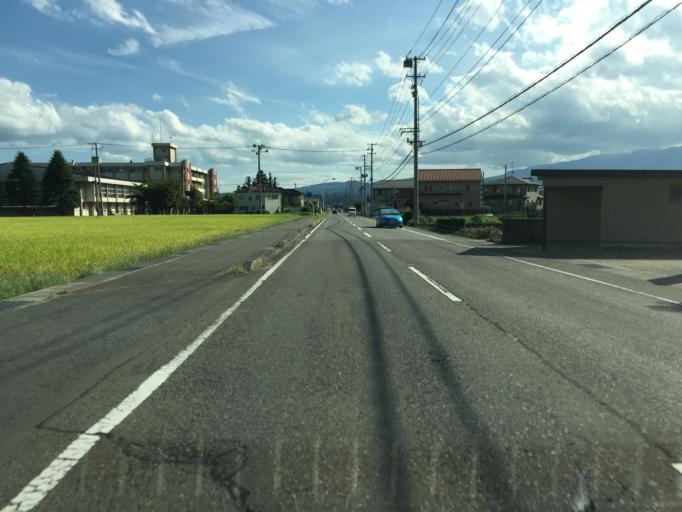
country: JP
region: Fukushima
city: Fukushima-shi
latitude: 37.7628
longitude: 140.4213
